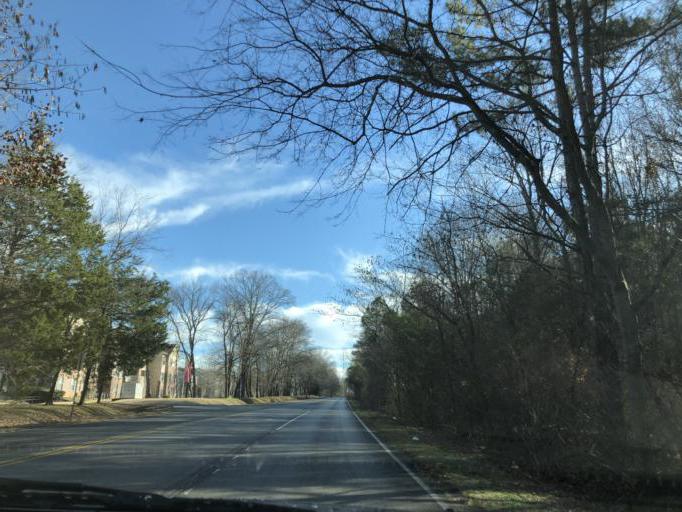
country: US
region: Tennessee
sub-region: Wilson County
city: Green Hill
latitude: 36.1657
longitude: -86.6082
